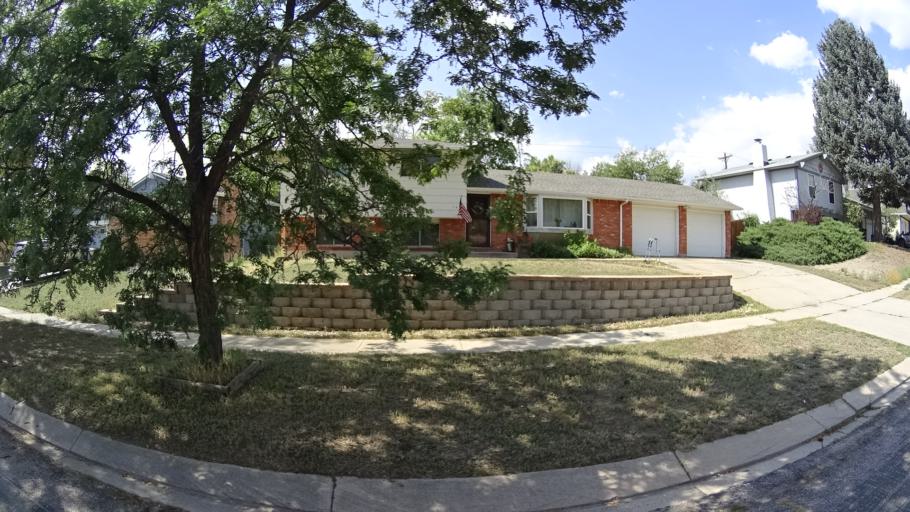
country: US
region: Colorado
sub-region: El Paso County
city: Colorado Springs
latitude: 38.8521
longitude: -104.7645
